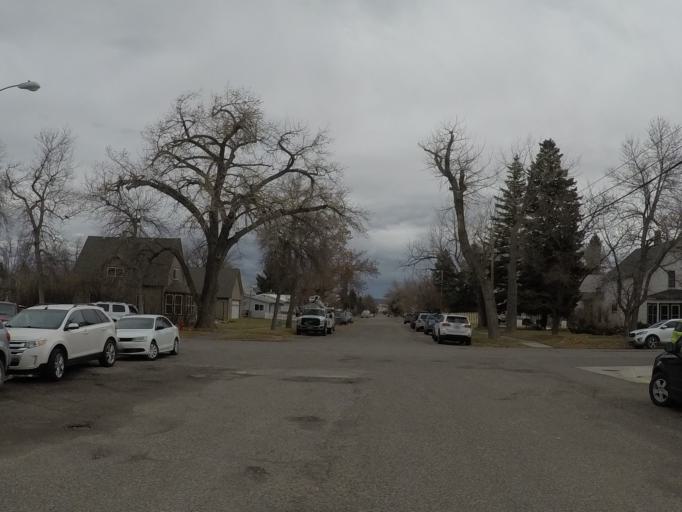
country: US
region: Montana
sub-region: Sweet Grass County
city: Big Timber
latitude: 45.8339
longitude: -109.9527
